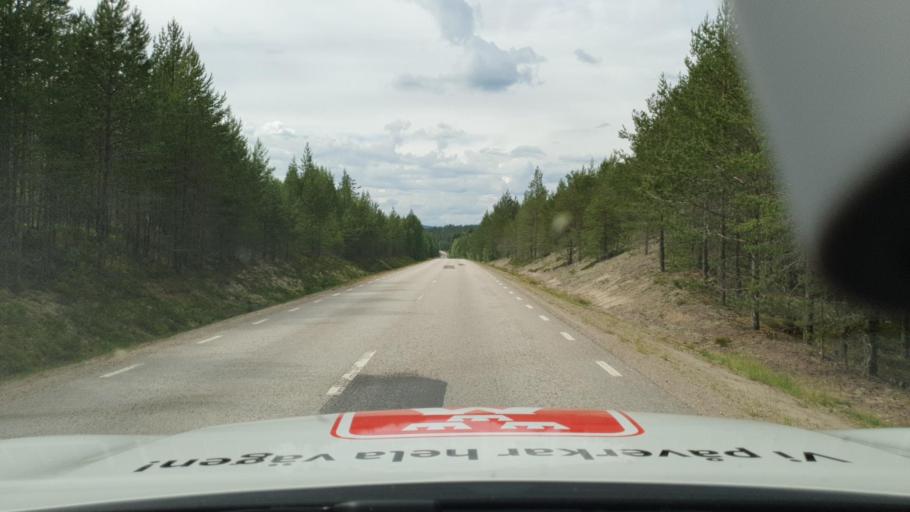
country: NO
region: Hedmark
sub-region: Trysil
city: Innbygda
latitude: 60.9239
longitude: 12.5249
